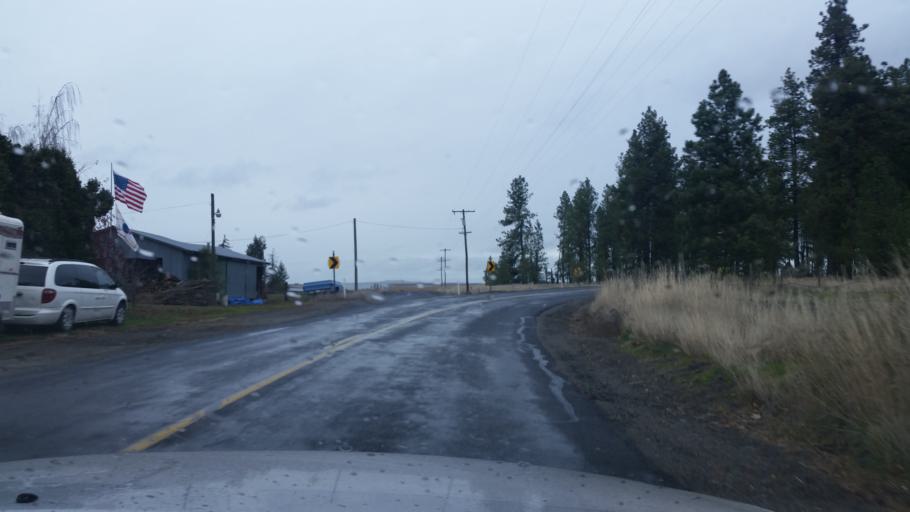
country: US
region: Washington
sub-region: Spokane County
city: Medical Lake
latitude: 47.6125
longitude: -117.7368
